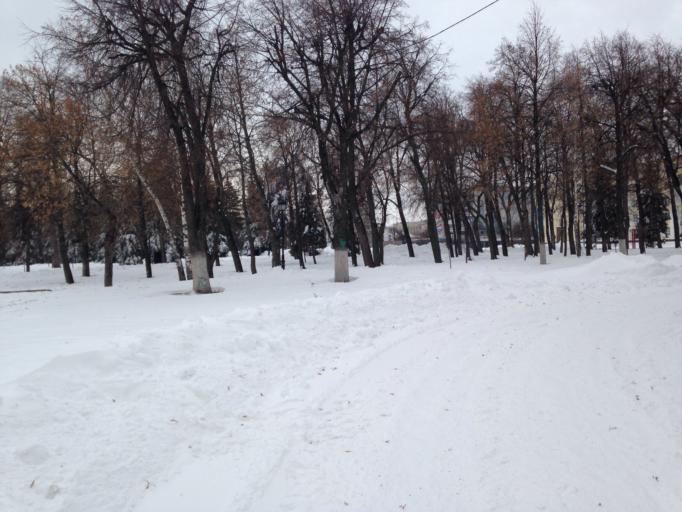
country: RU
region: Ulyanovsk
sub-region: Ulyanovskiy Rayon
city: Ulyanovsk
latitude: 54.3145
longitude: 48.4054
